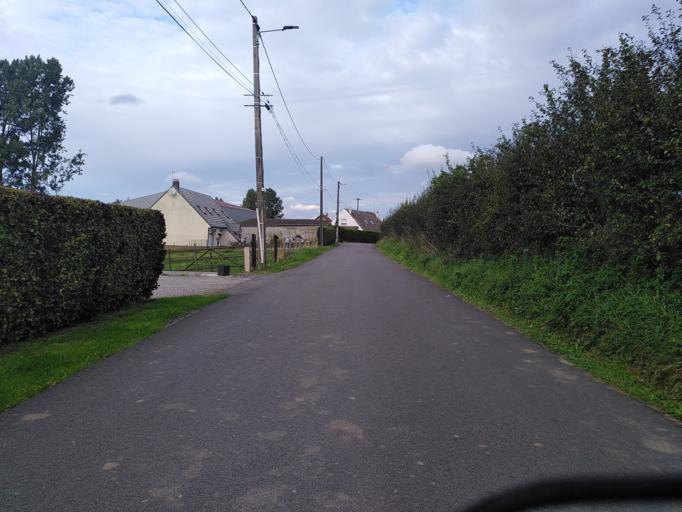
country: FR
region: Nord-Pas-de-Calais
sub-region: Departement du Pas-de-Calais
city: Therouanne
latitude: 50.6328
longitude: 2.2541
